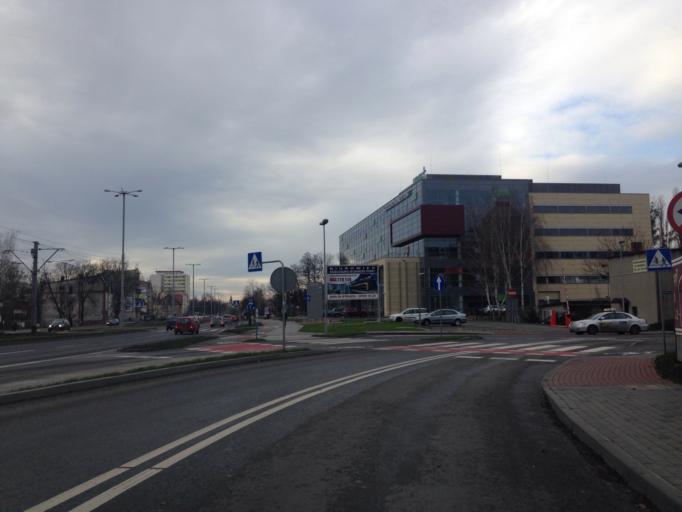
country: PL
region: Kujawsko-Pomorskie
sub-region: Torun
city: Torun
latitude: 53.0252
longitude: 18.6273
